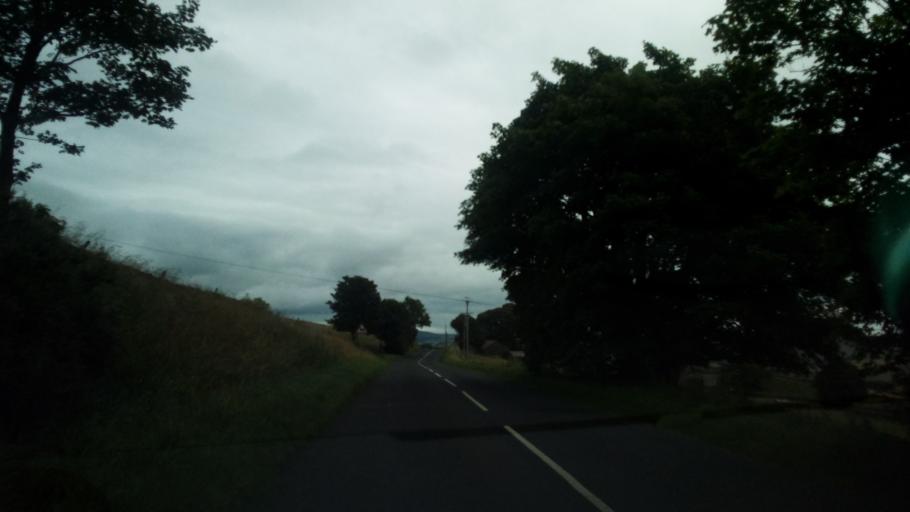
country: GB
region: England
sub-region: County Durham
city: Holwick
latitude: 54.5943
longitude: -2.1275
